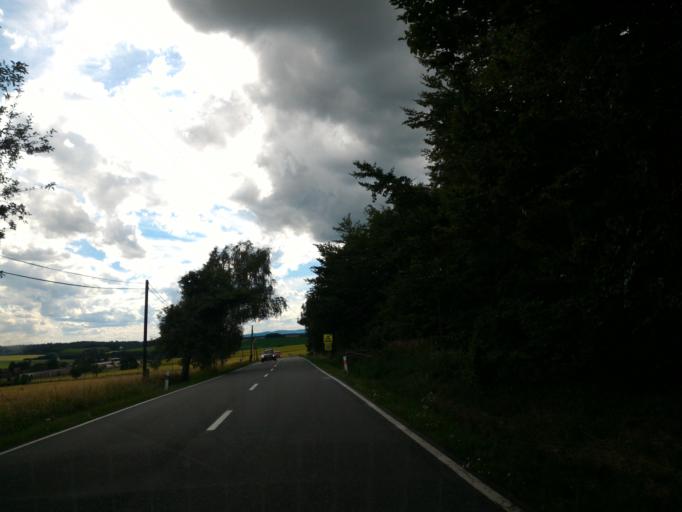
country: CZ
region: Vysocina
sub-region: Okres Jihlava
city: Polna
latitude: 49.4504
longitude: 15.7815
